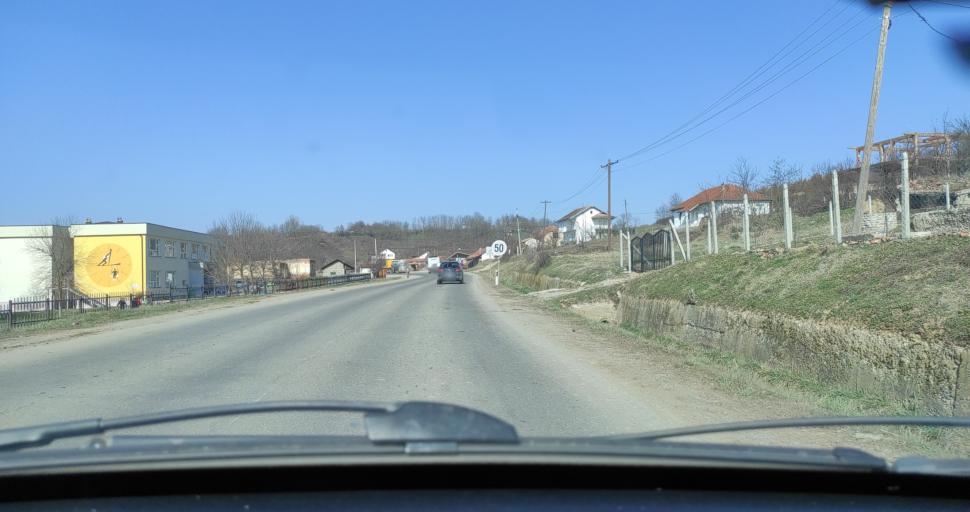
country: XK
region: Pec
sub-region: Komuna e Klines
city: Klina
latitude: 42.6038
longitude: 20.5207
